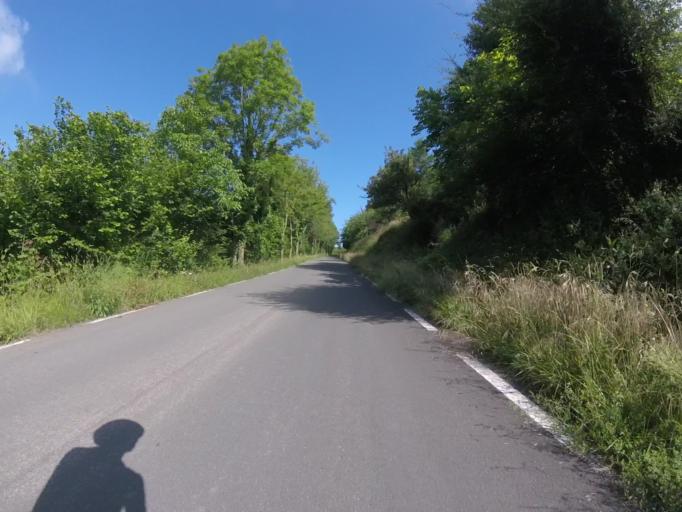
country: ES
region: Basque Country
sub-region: Provincia de Guipuzcoa
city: Ormaiztegui
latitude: 43.0839
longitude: -2.2405
